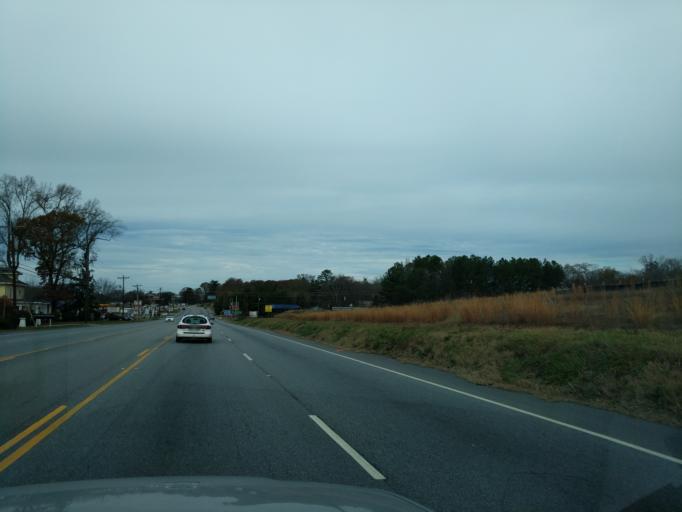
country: US
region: South Carolina
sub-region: Anderson County
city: Pendleton
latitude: 34.5931
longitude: -82.7478
